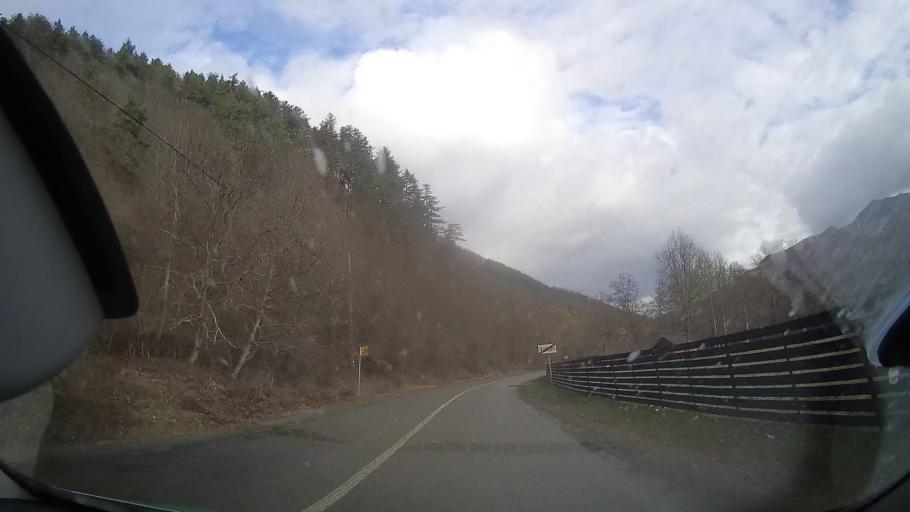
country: RO
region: Alba
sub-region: Comuna Ocolis
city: Ocolis
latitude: 46.4805
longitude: 23.5080
